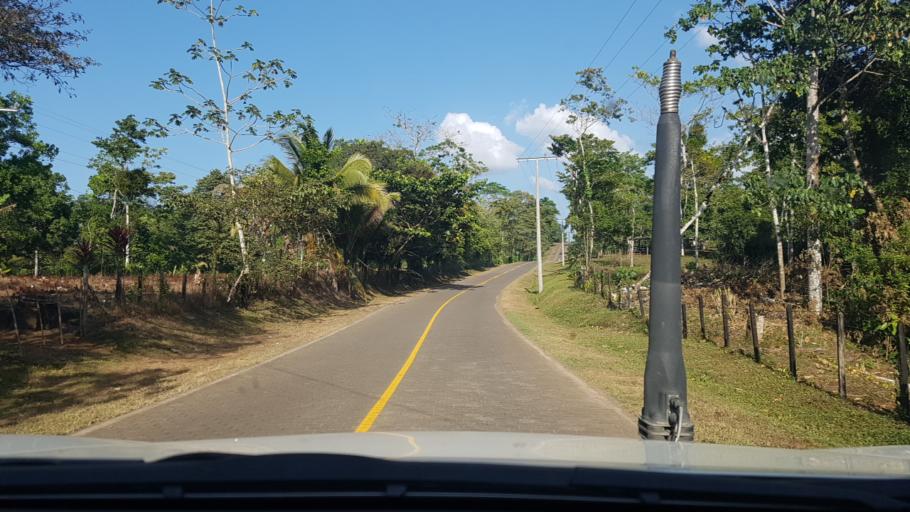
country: NI
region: Atlantico Sur
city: Nueva Guinea
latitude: 11.6883
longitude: -84.4317
